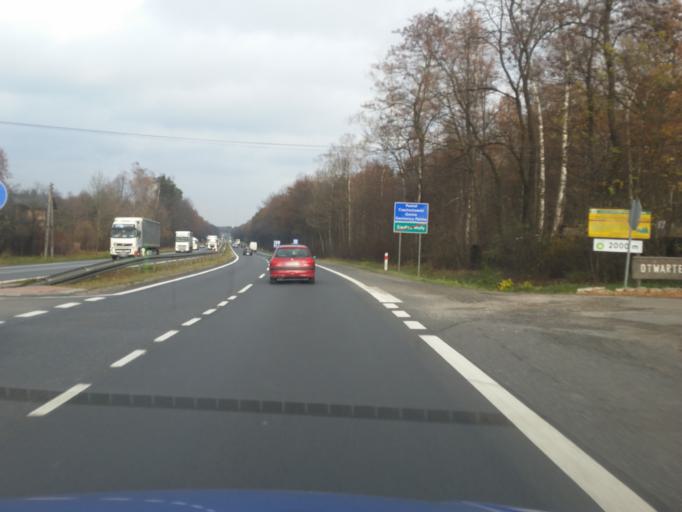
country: PL
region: Silesian Voivodeship
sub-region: Powiat czestochowski
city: Kamienica Polska
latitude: 50.6413
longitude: 19.1360
